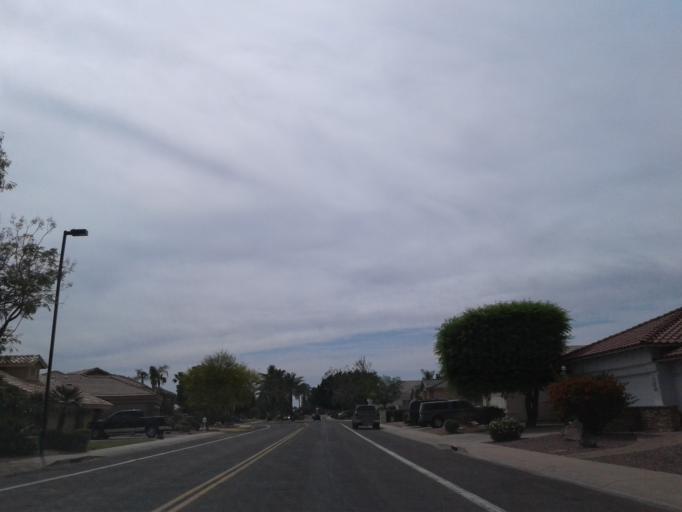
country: US
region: Arizona
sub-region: Maricopa County
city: Peoria
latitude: 33.6831
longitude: -112.1845
